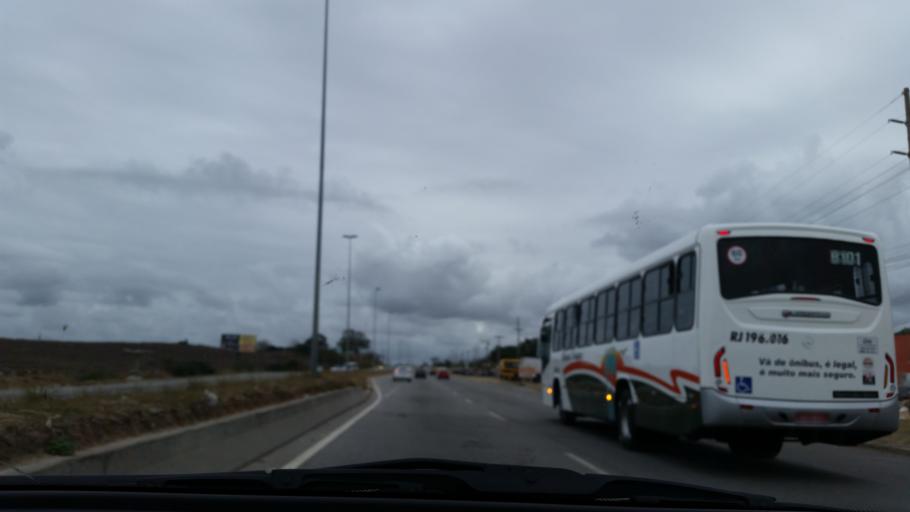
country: BR
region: Rio de Janeiro
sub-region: Sao Pedro Da Aldeia
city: Sao Pedro da Aldeia
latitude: -22.8392
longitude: -42.0742
